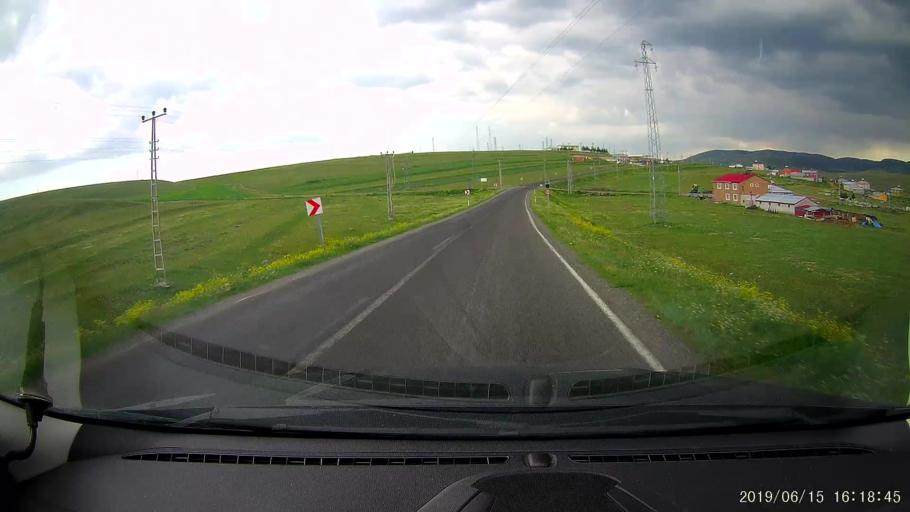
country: TR
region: Ardahan
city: Hanak
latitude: 41.2360
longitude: 42.8533
